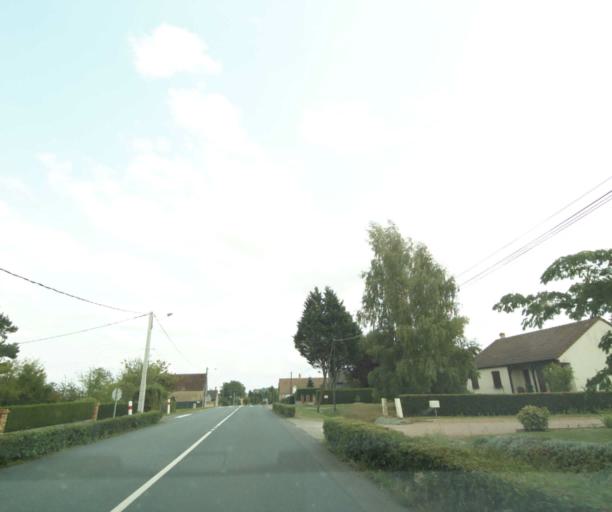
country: FR
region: Centre
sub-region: Departement de l'Indre
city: Buzancais
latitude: 46.8829
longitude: 1.4474
